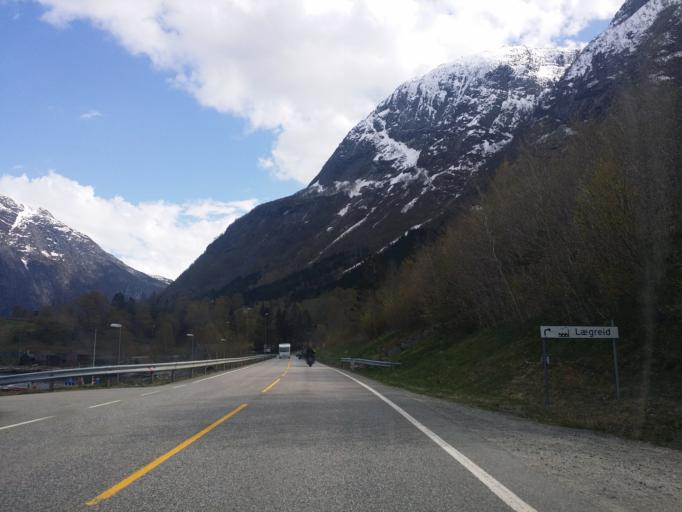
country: NO
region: Hordaland
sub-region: Eidfjord
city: Eidfjord
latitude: 60.4651
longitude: 7.0562
